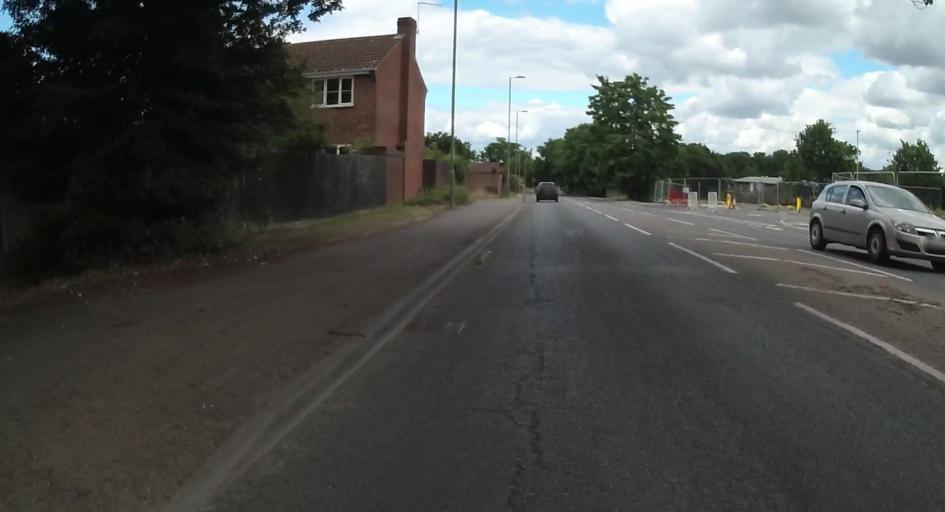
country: GB
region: England
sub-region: Hampshire
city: Fleet
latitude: 51.2578
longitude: -0.8263
